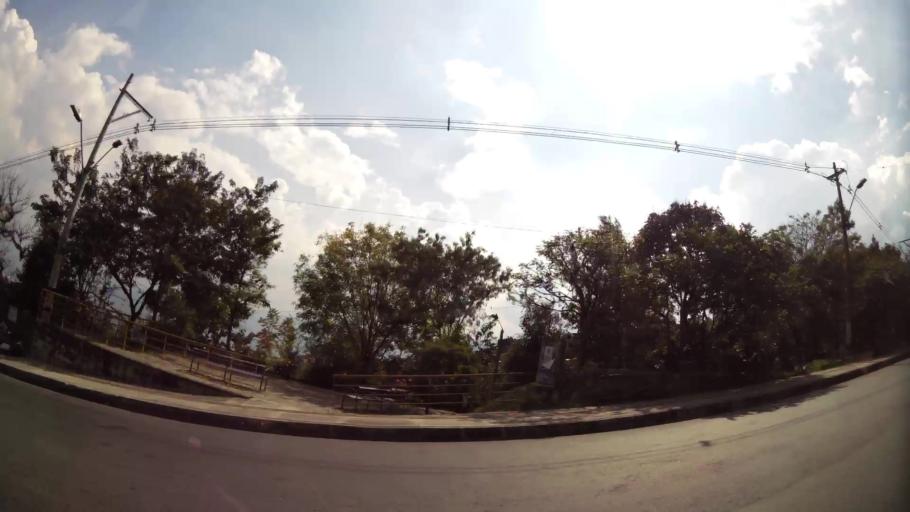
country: CO
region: Antioquia
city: Medellin
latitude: 6.2886
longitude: -75.5903
